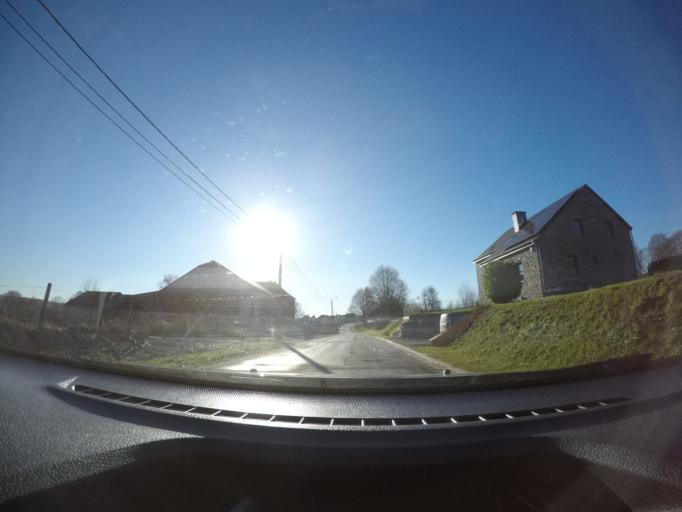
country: BE
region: Wallonia
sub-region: Province du Luxembourg
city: Bertrix
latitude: 49.8408
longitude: 5.3245
